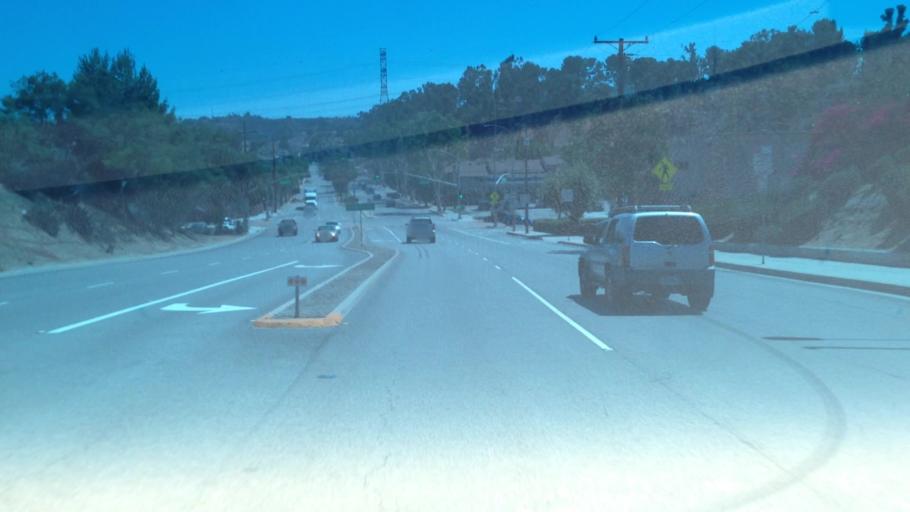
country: US
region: California
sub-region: Los Angeles County
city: South San Gabriel
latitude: 34.0427
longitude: -118.0913
